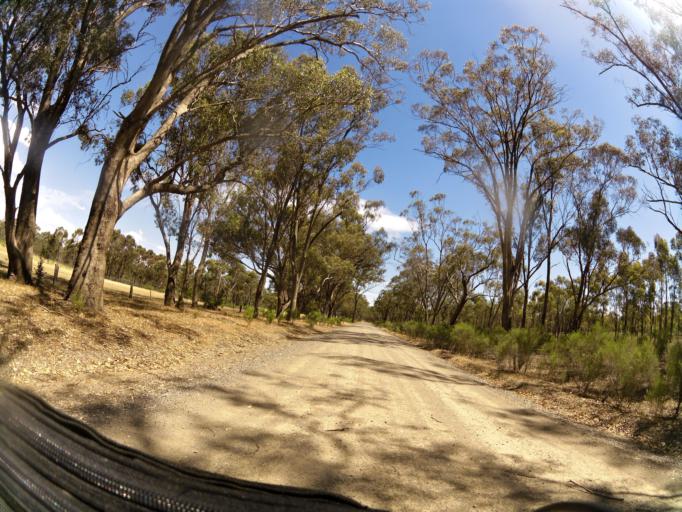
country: AU
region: Victoria
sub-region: Campaspe
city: Kyabram
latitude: -36.8200
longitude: 145.0799
